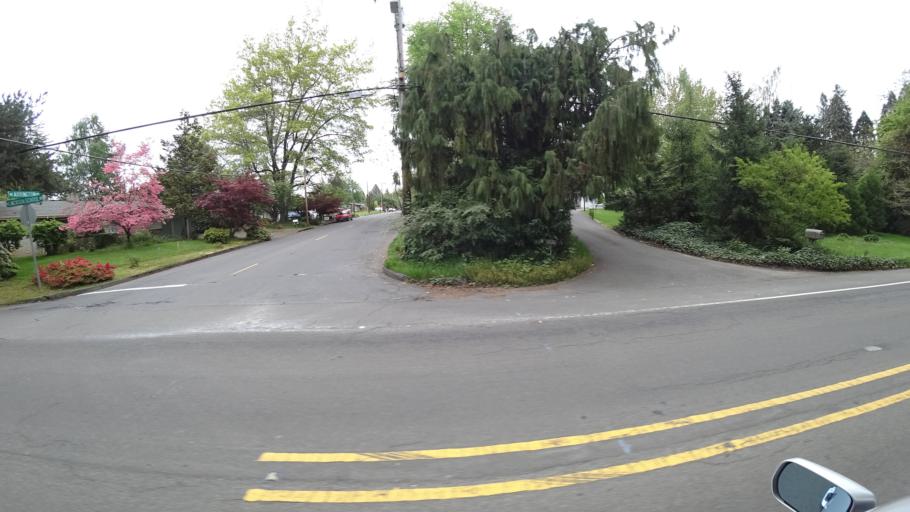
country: US
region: Oregon
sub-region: Washington County
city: Hillsboro
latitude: 45.5327
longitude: -122.9797
